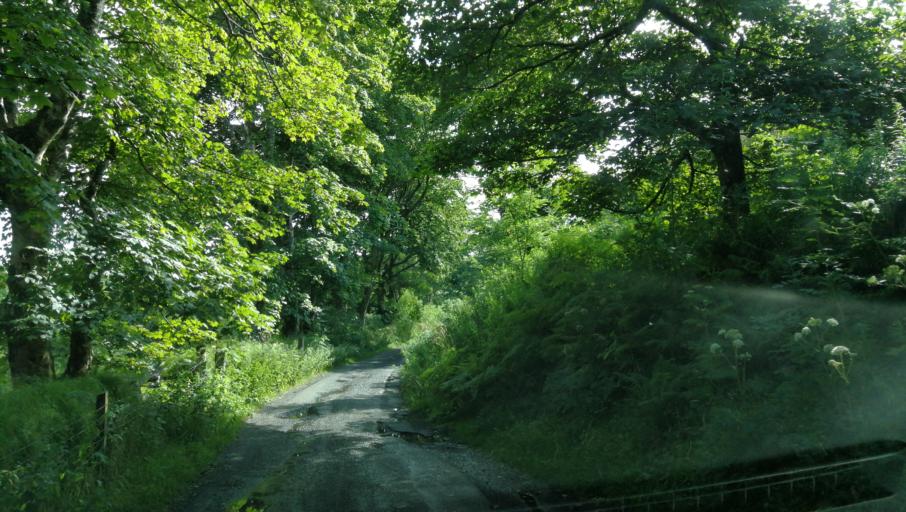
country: GB
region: Scotland
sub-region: Highland
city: Isle of Skye
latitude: 57.3989
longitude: -6.5679
